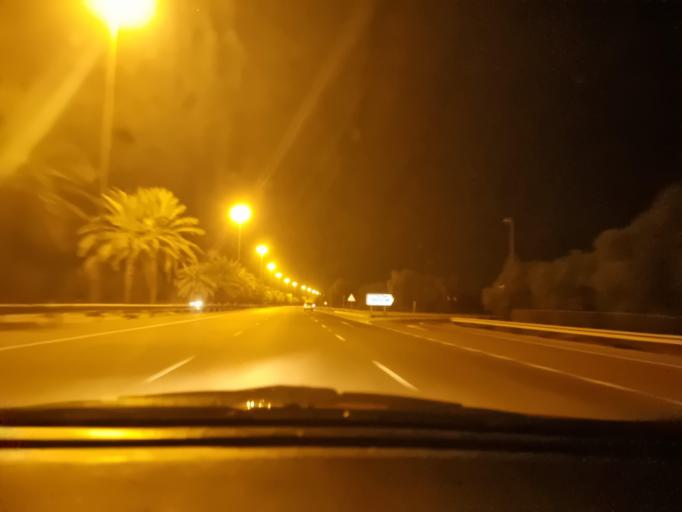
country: AE
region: Abu Dhabi
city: Al Ain
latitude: 24.1706
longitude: 55.2831
